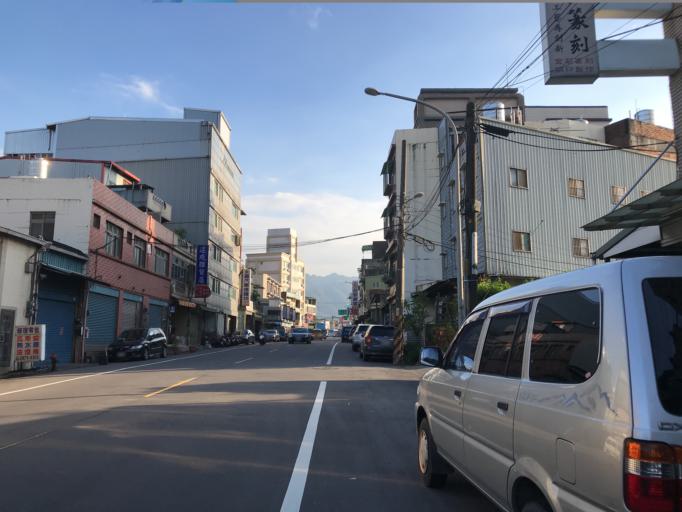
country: TW
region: Taiwan
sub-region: Taoyuan
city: Taoyuan
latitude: 24.9209
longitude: 121.3670
